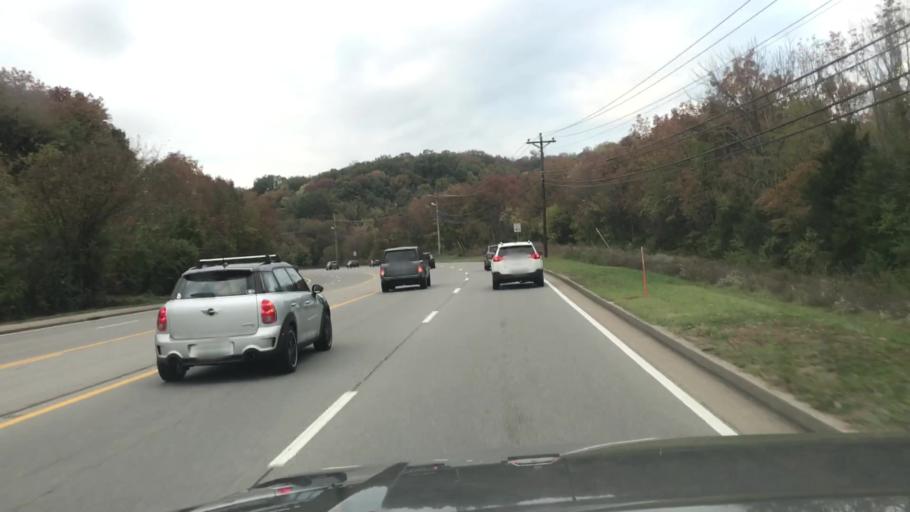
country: US
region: Tennessee
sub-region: Williamson County
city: Franklin
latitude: 35.9691
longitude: -86.8196
